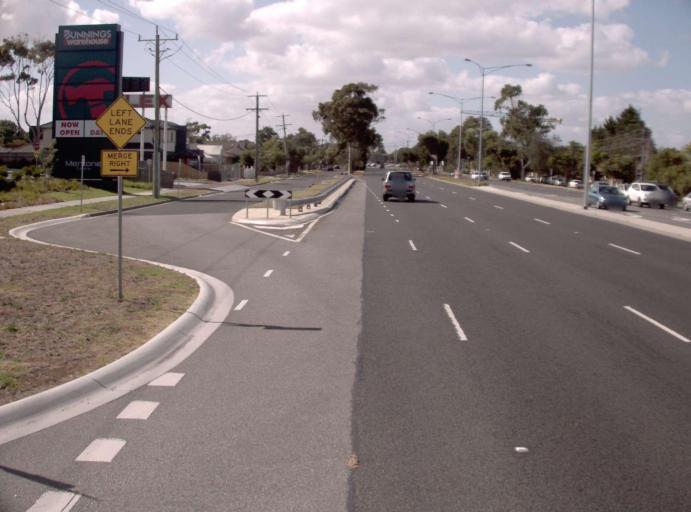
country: AU
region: Victoria
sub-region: Kingston
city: Mentone
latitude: -37.9773
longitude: 145.0673
